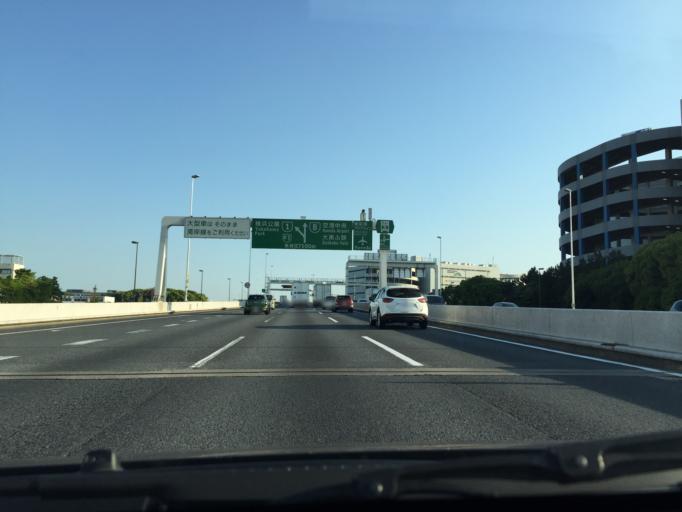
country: JP
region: Kanagawa
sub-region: Kawasaki-shi
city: Kawasaki
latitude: 35.5879
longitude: 139.7553
